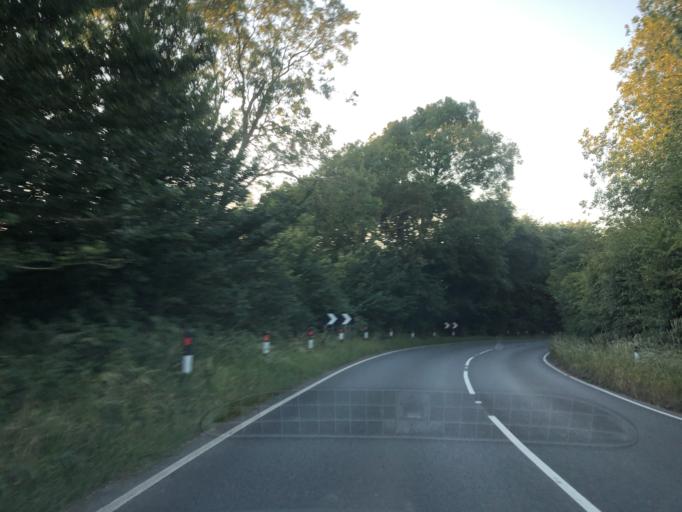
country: GB
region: England
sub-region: Isle of Wight
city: Newport
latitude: 50.6577
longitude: -1.2852
